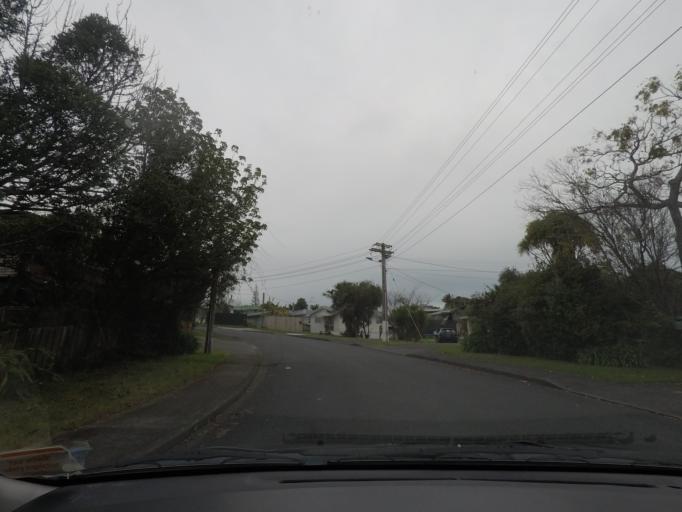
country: NZ
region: Auckland
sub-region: Auckland
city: Rosebank
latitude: -36.8608
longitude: 174.6398
